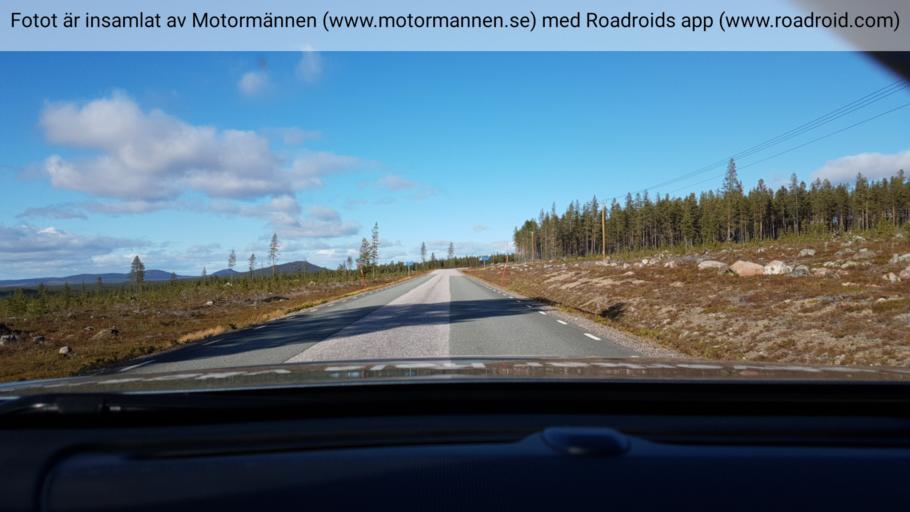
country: SE
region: Vaesterbotten
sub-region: Mala Kommun
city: Mala
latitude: 65.7752
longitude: 18.5202
